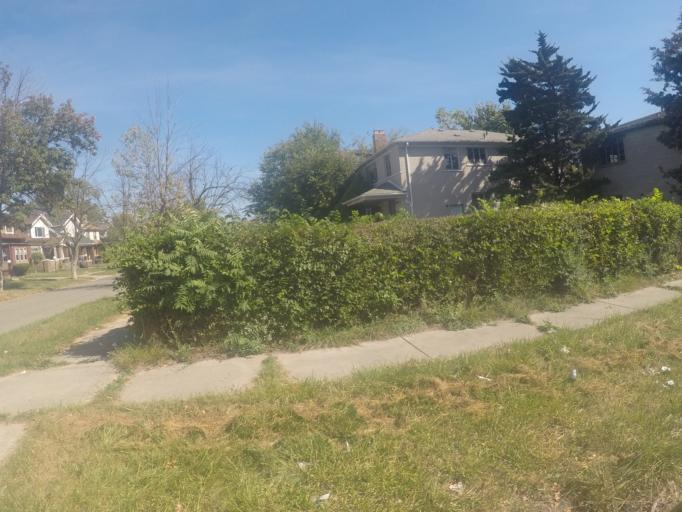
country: US
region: Michigan
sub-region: Wayne County
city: Highland Park
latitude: 42.3603
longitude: -83.1316
